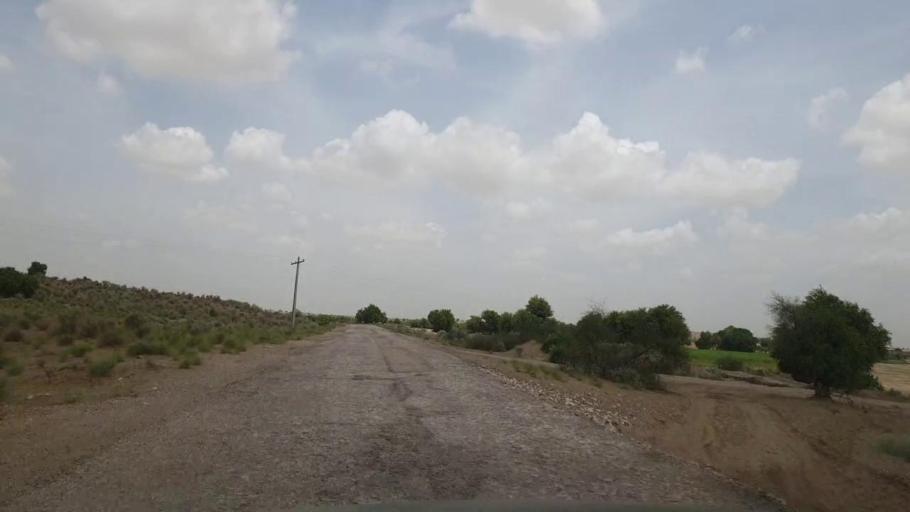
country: PK
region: Sindh
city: Kot Diji
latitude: 27.2006
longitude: 69.1256
